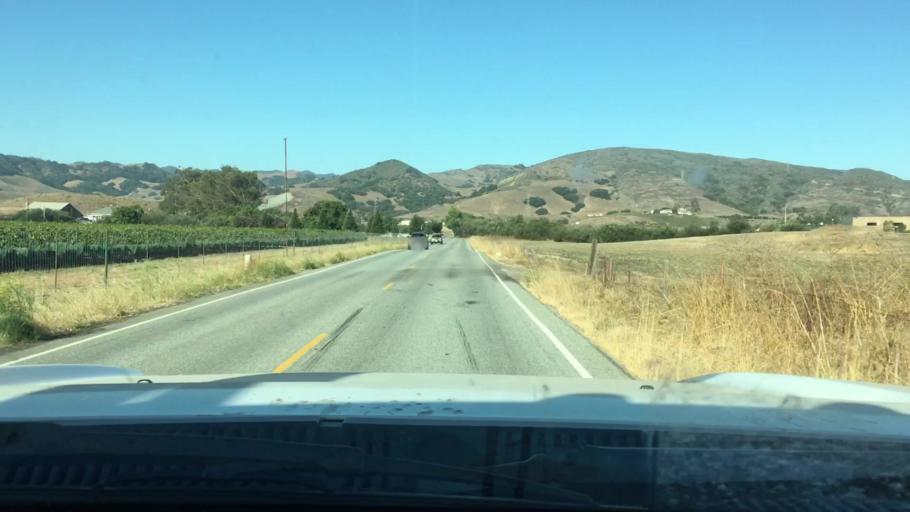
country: US
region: California
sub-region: San Luis Obispo County
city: San Luis Obispo
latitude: 35.2366
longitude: -120.6673
